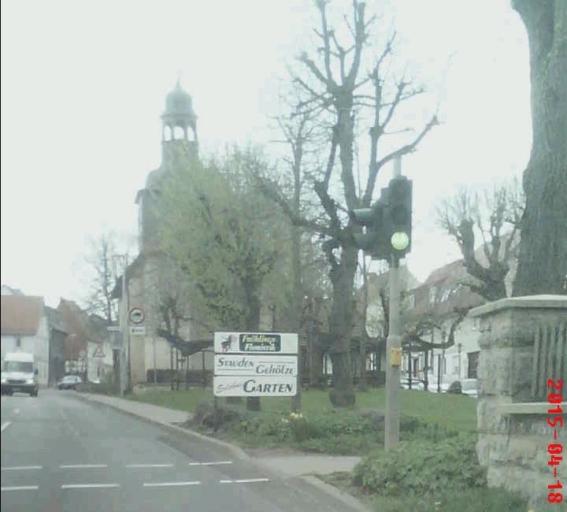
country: DE
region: Thuringia
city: Hausen
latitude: 51.3856
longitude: 10.3568
